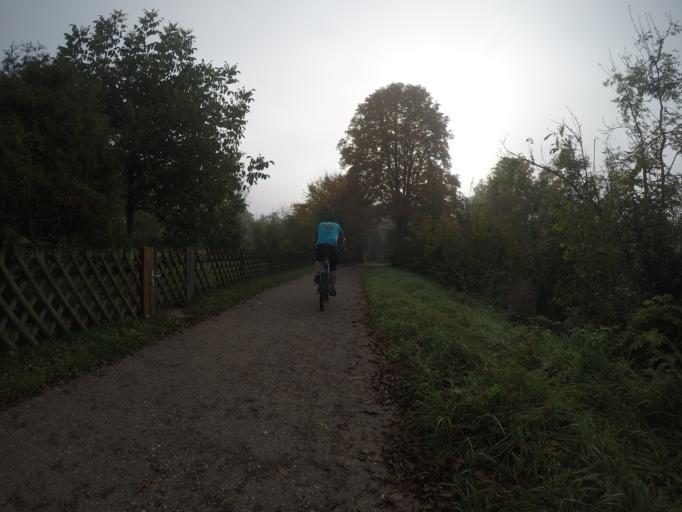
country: DE
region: Baden-Wuerttemberg
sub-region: Regierungsbezirk Stuttgart
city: Ostfildern
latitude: 48.7088
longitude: 9.2646
